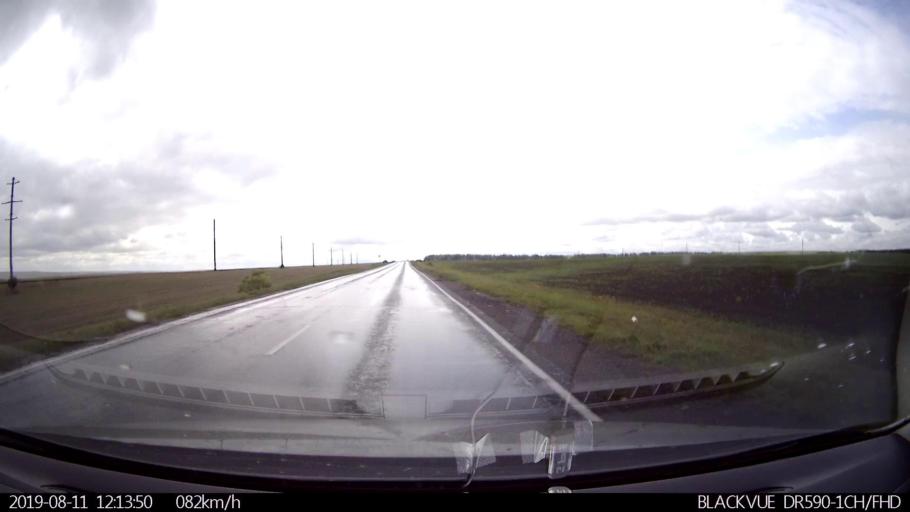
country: RU
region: Ulyanovsk
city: Ignatovka
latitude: 53.9580
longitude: 47.9879
